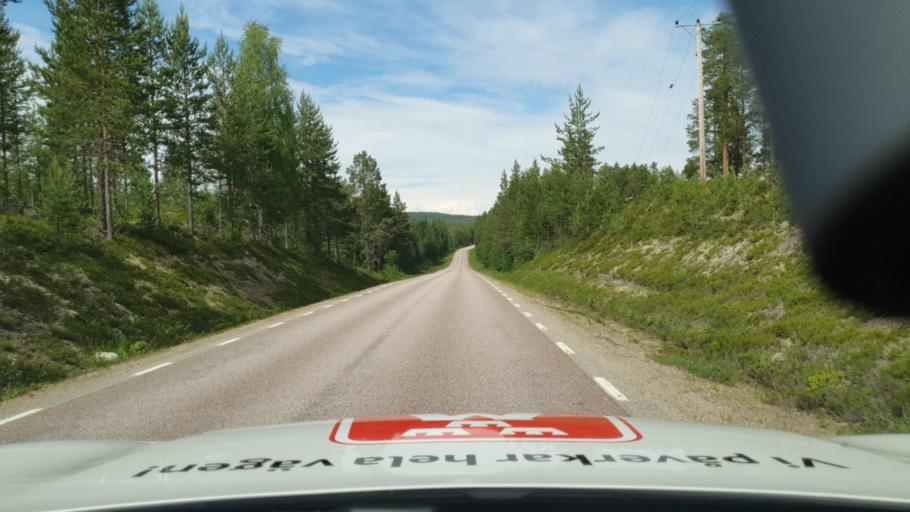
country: NO
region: Hedmark
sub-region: Asnes
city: Flisa
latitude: 60.7208
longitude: 12.6185
